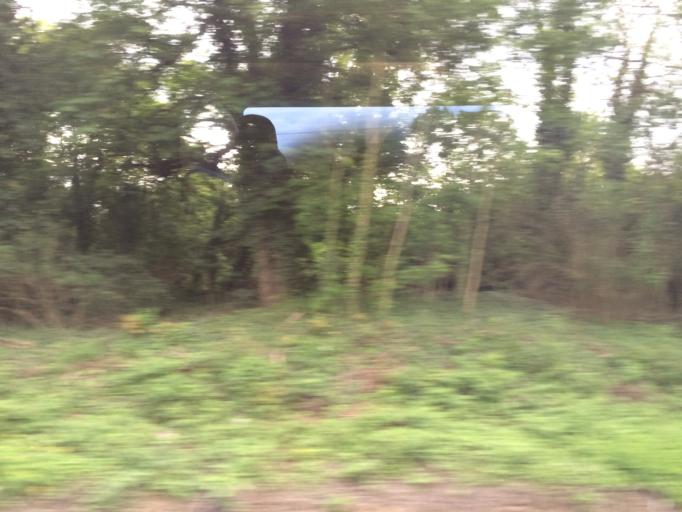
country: DE
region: Hesse
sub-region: Regierungsbezirk Darmstadt
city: Hanau am Main
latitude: 50.1258
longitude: 8.9181
